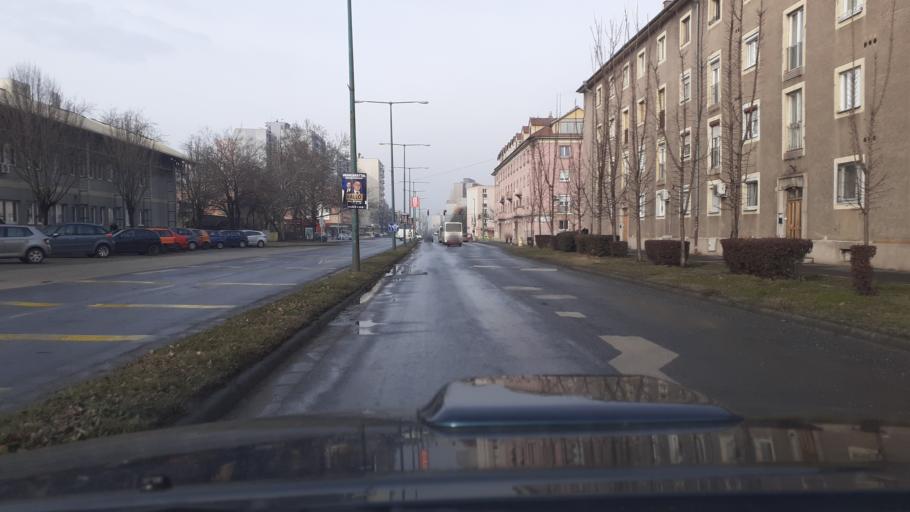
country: HU
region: Fejer
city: Dunaujvaros
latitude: 46.9608
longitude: 18.9350
